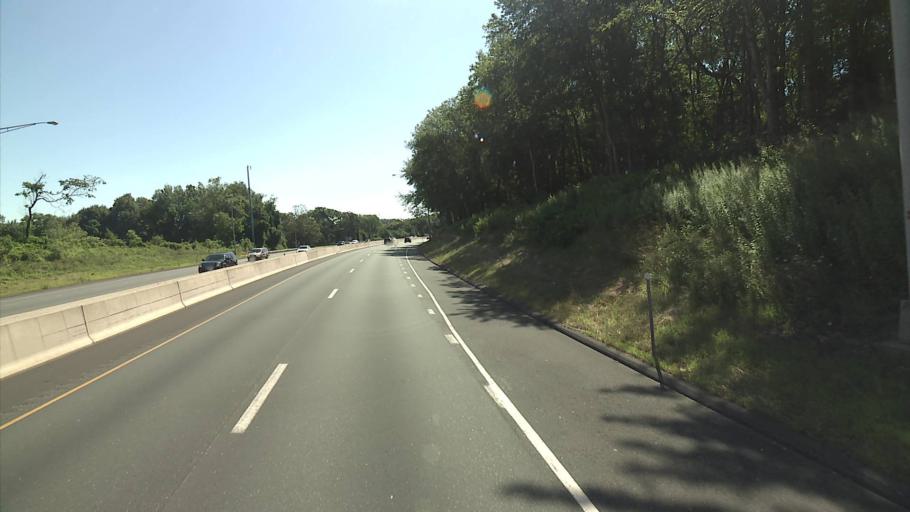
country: US
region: Connecticut
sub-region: New London County
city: Central Waterford
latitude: 41.3712
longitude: -72.1274
